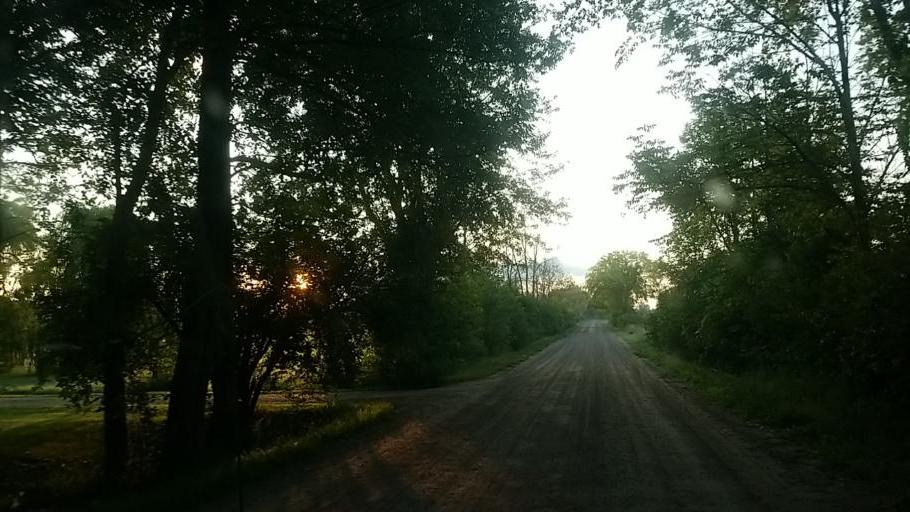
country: US
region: Michigan
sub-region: Osceola County
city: Evart
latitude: 43.9152
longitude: -85.1970
